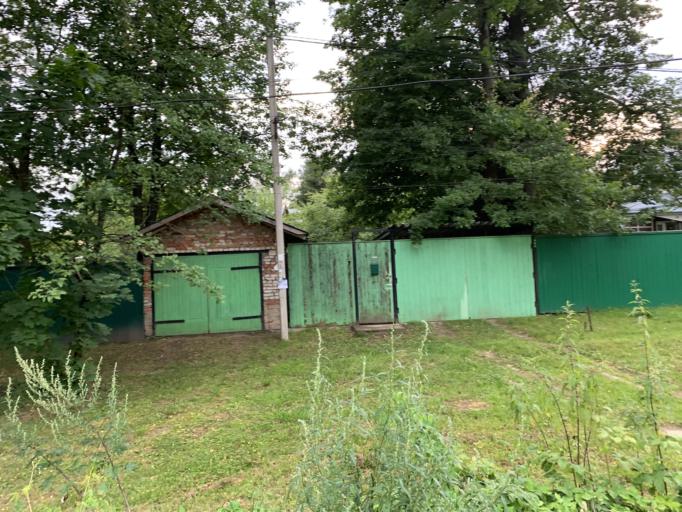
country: RU
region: Moskovskaya
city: Mamontovka
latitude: 55.9743
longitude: 37.8333
